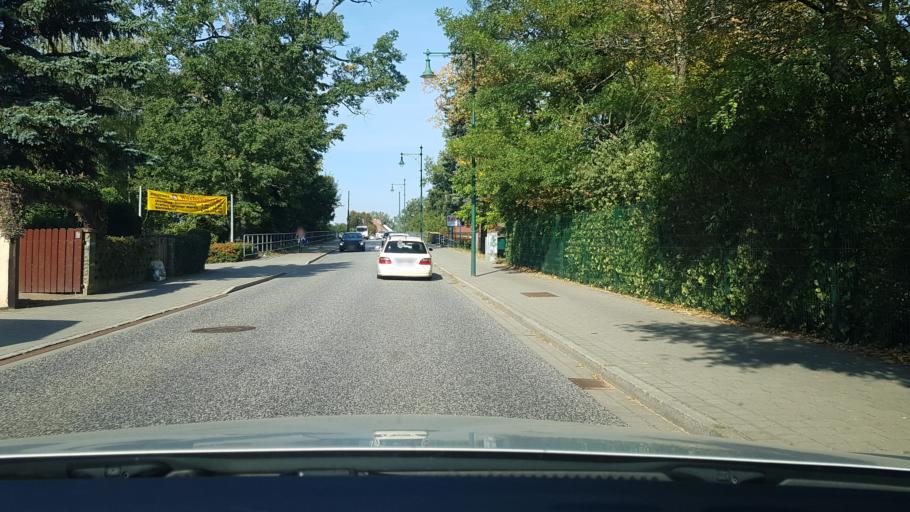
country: DE
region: Brandenburg
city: Beeskow
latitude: 52.1685
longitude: 14.2560
